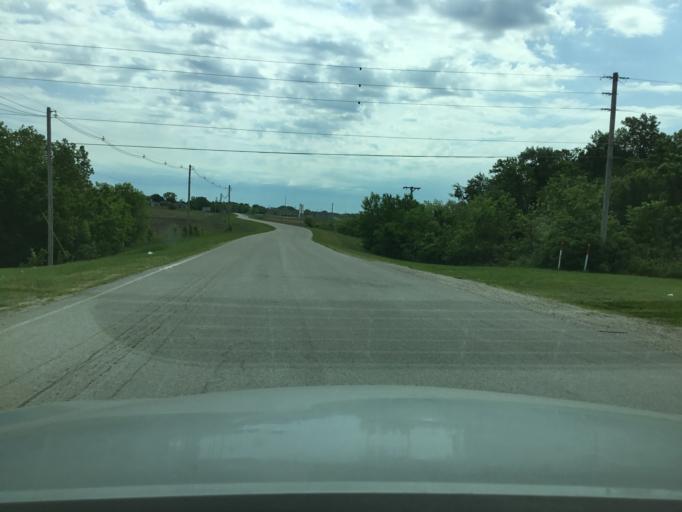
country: US
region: Kansas
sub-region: Montgomery County
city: Coffeyville
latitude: 37.0074
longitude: -95.6159
